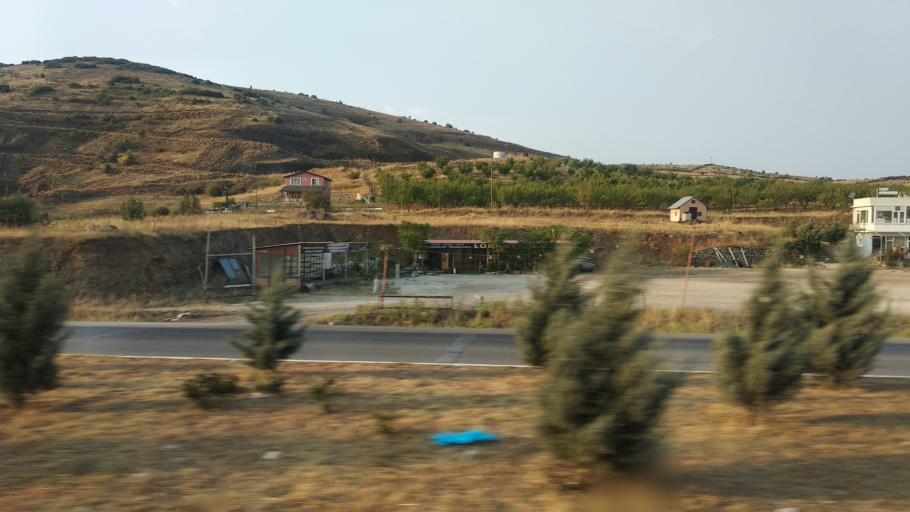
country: TR
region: Manisa
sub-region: Kula
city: Kula
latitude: 38.5680
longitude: 28.5765
